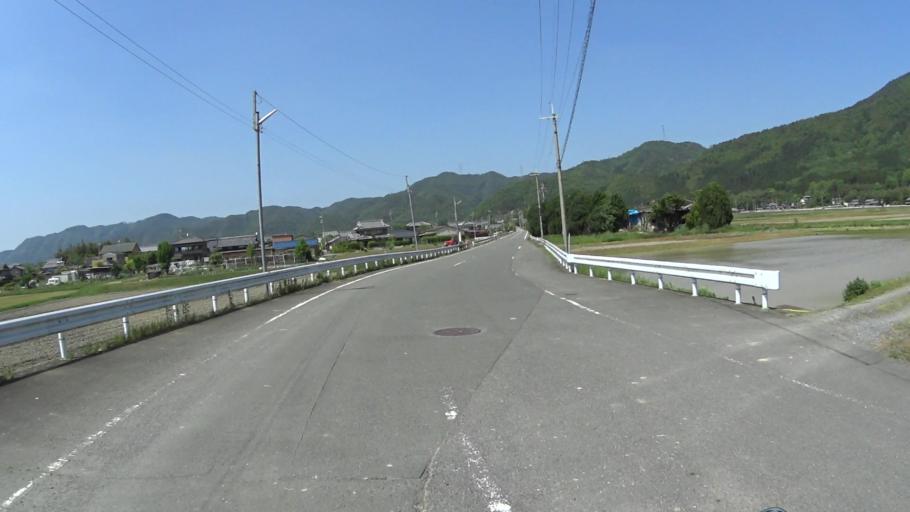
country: JP
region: Kyoto
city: Kameoka
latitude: 35.0712
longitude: 135.5614
